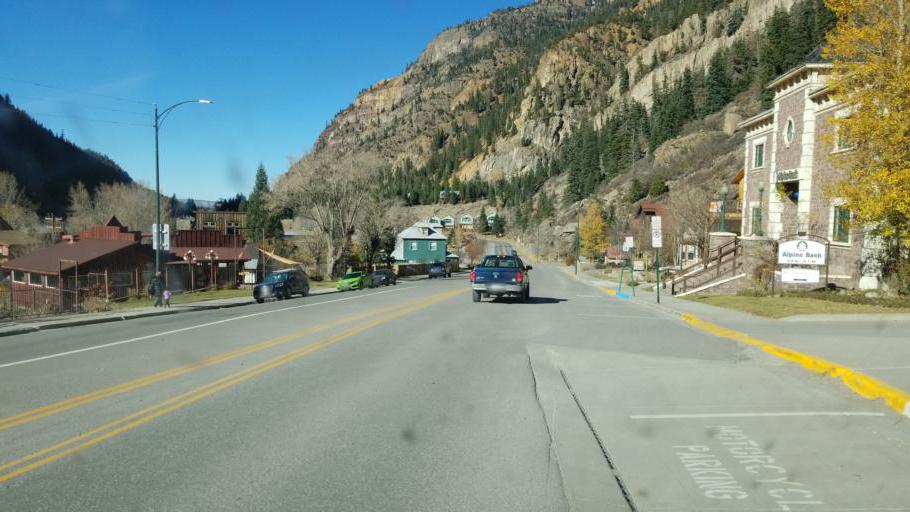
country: US
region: Colorado
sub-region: Ouray County
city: Ouray
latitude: 38.0261
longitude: -107.6714
